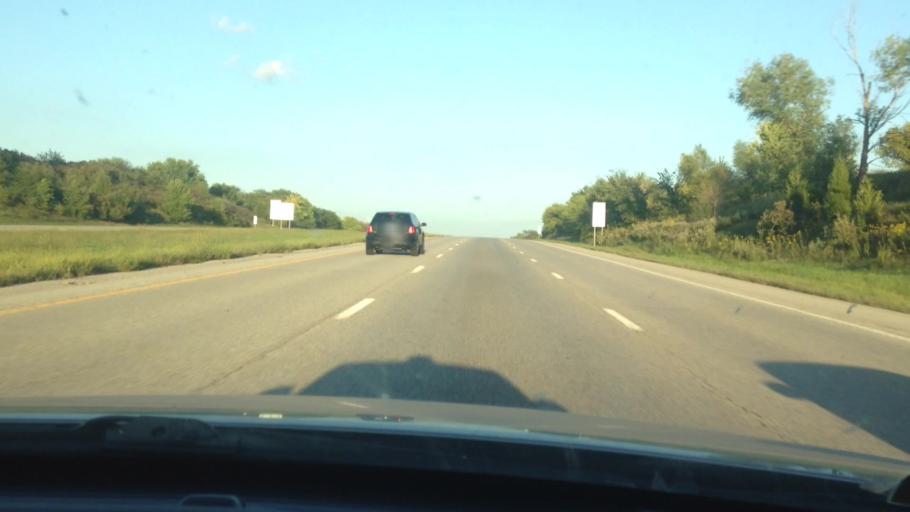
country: US
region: Missouri
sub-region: Platte County
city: Weatherby Lake
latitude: 39.3074
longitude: -94.6386
